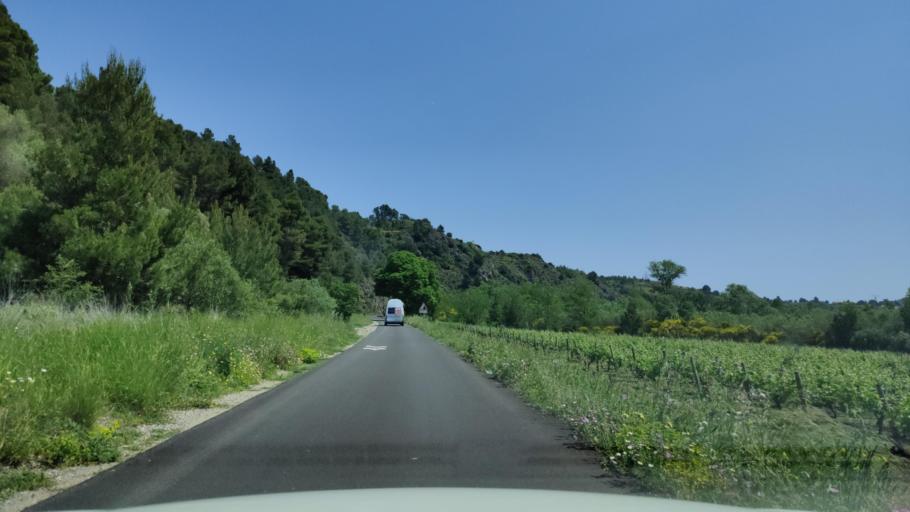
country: FR
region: Languedoc-Roussillon
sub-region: Departement des Pyrenees-Orientales
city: Baixas
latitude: 42.7841
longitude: 2.7681
